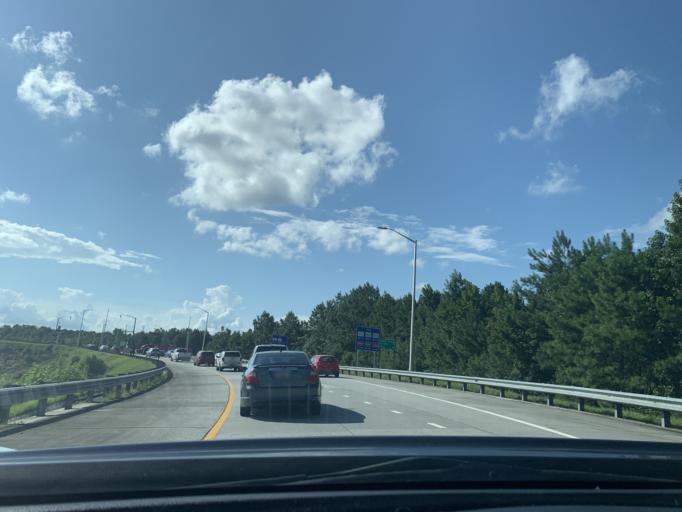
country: US
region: Georgia
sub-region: Chatham County
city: Pooler
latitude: 32.0847
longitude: -81.2772
